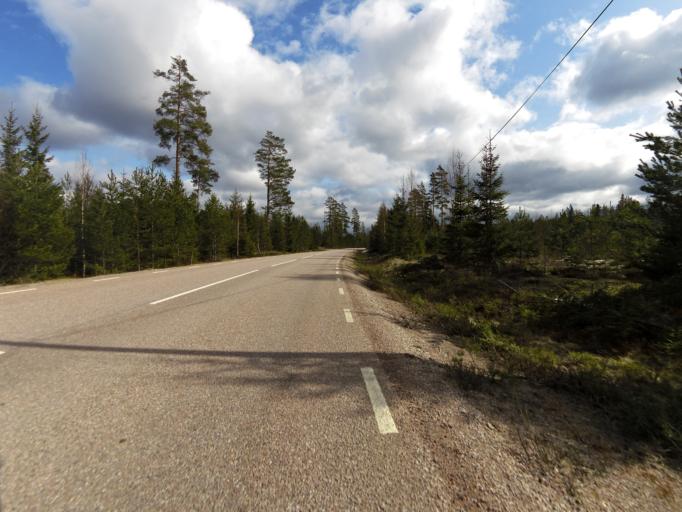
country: SE
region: Dalarna
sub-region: Avesta Kommun
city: Horndal
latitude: 60.3061
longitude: 16.2552
